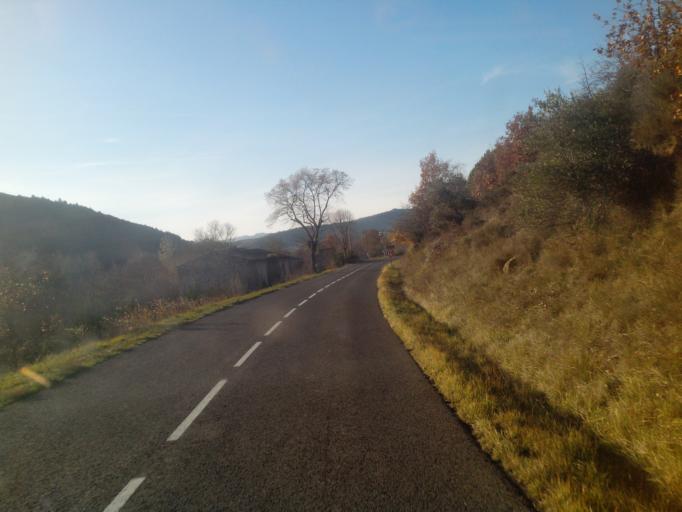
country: FR
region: Languedoc-Roussillon
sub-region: Departement de l'Aude
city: Couiza
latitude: 42.9401
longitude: 2.2686
